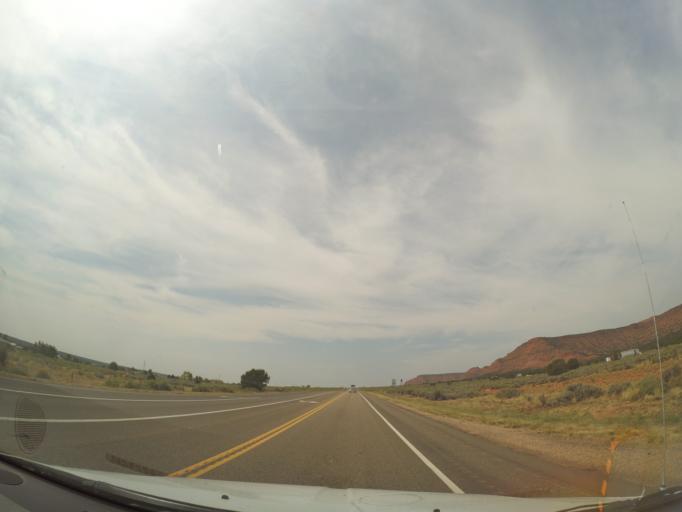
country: US
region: Utah
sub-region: Kane County
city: Kanab
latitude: 37.0341
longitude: -112.3860
